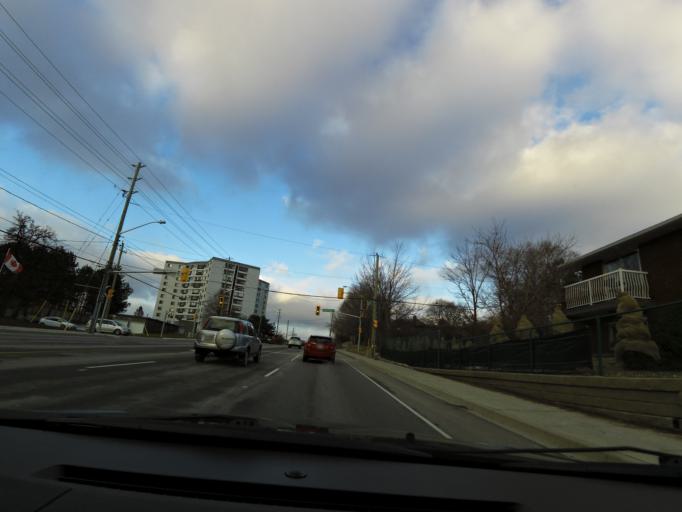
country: CA
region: Ontario
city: Waterloo
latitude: 43.4813
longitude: -80.5121
